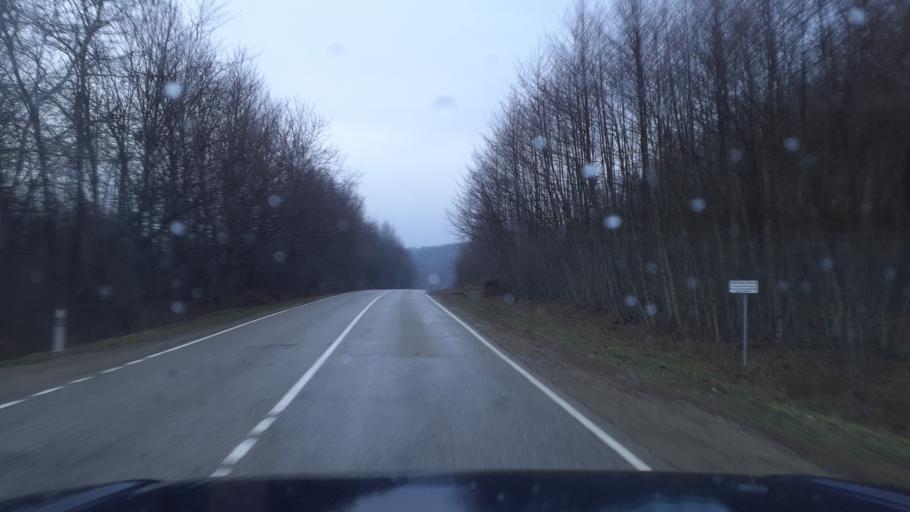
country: RU
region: Krasnodarskiy
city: Neftegorsk
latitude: 44.3152
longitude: 39.8327
